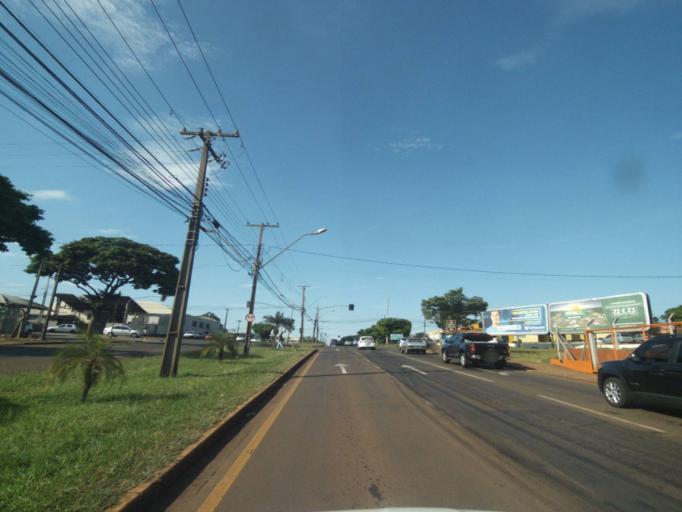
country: BR
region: Parana
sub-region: Londrina
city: Londrina
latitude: -23.3586
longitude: -51.1508
